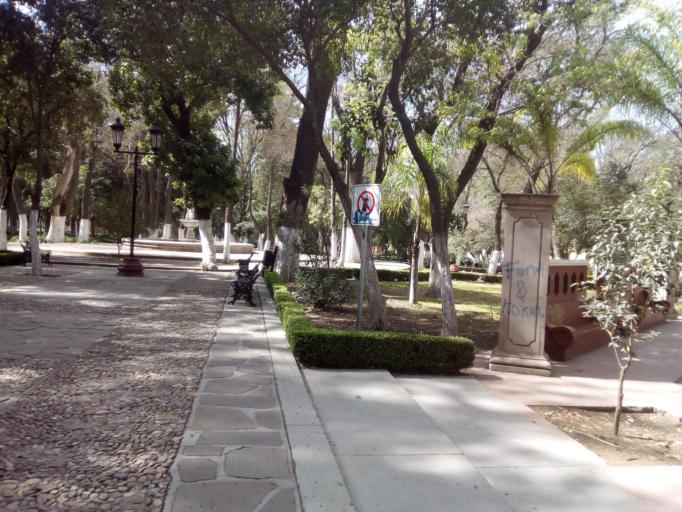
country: MX
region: Guanajuato
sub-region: San Luis de la Paz
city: San Luis de la Paz
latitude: 21.2989
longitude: -100.5096
